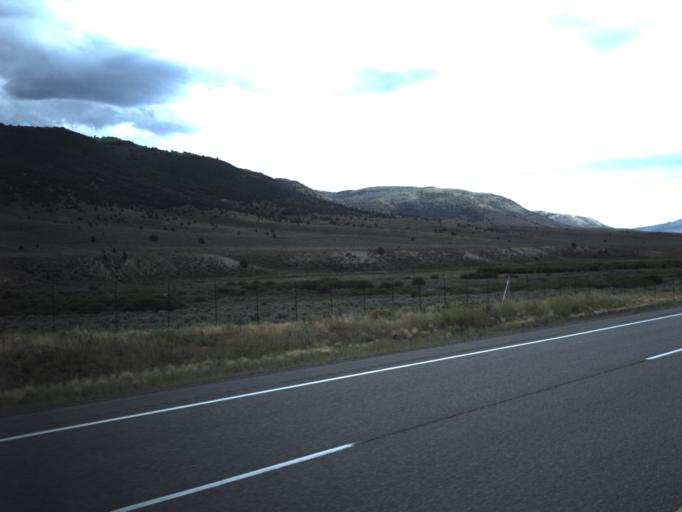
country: US
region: Utah
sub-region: Carbon County
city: Helper
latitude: 39.9159
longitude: -111.0636
